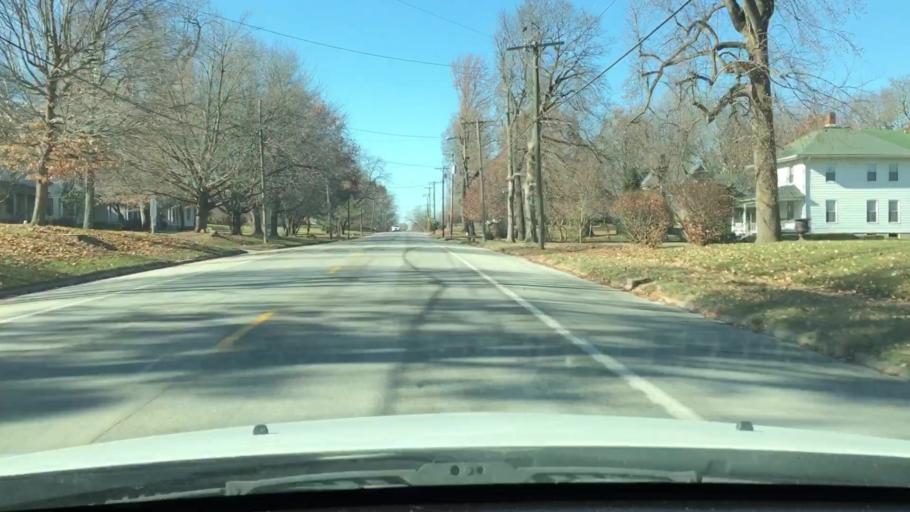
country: US
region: Illinois
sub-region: Pike County
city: Pittsfield
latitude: 39.6068
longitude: -90.7973
